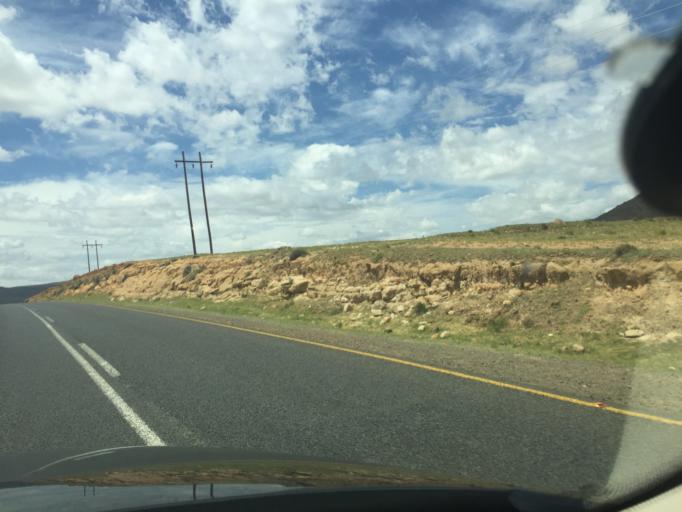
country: LS
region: Mafeteng
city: Mafeteng
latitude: -29.9283
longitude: 27.2578
